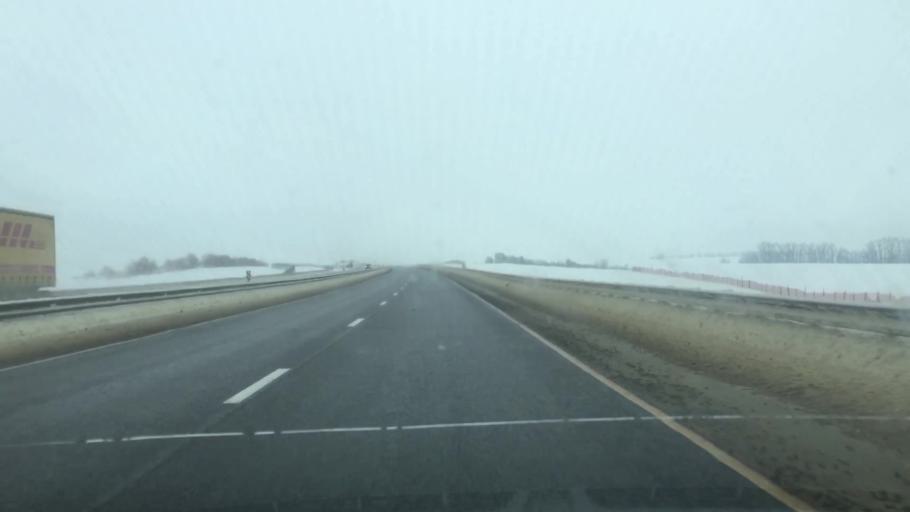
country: RU
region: Tula
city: Yefremov
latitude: 53.2239
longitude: 38.2094
